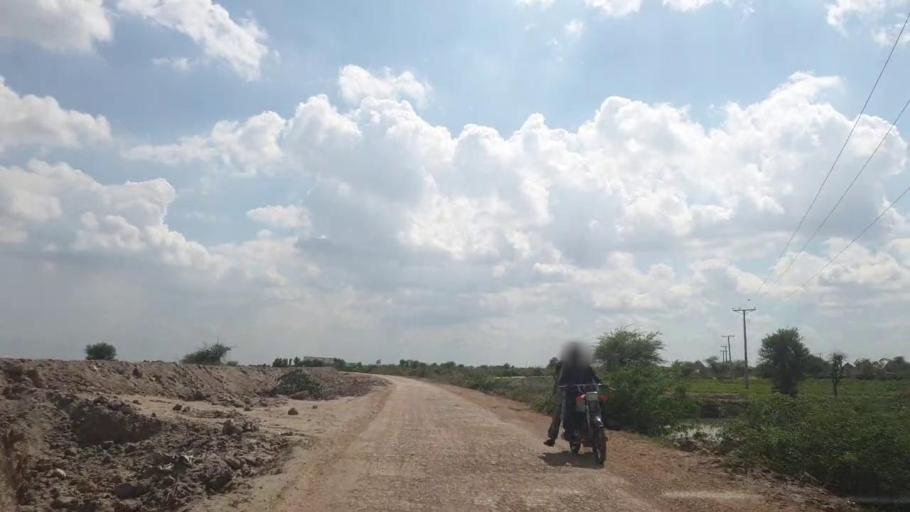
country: PK
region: Sindh
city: Pithoro
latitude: 25.5915
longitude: 69.3967
